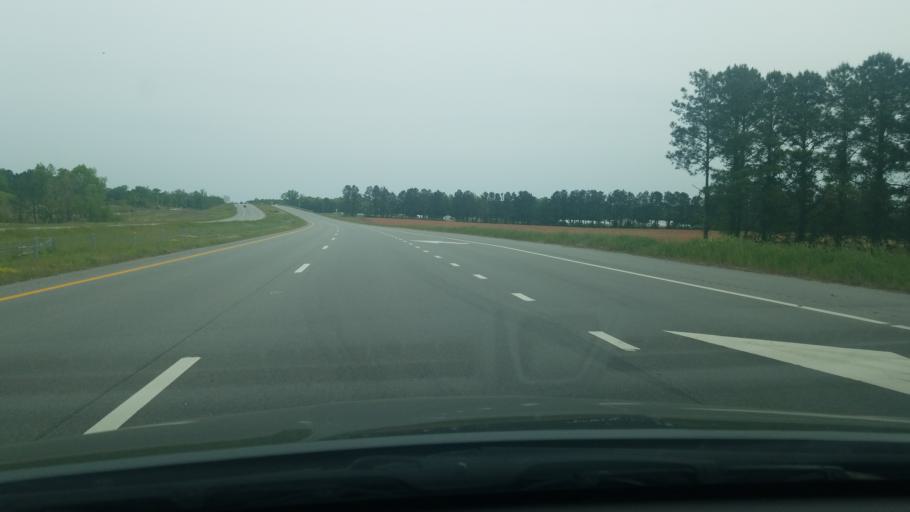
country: US
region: North Carolina
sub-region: Jones County
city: Maysville
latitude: 35.0050
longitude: -77.2301
